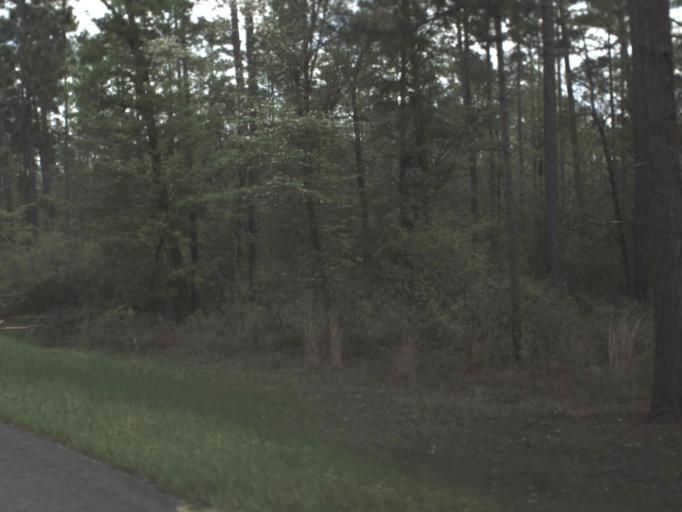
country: US
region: Florida
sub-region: Okaloosa County
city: Crestview
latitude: 30.9016
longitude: -86.6575
